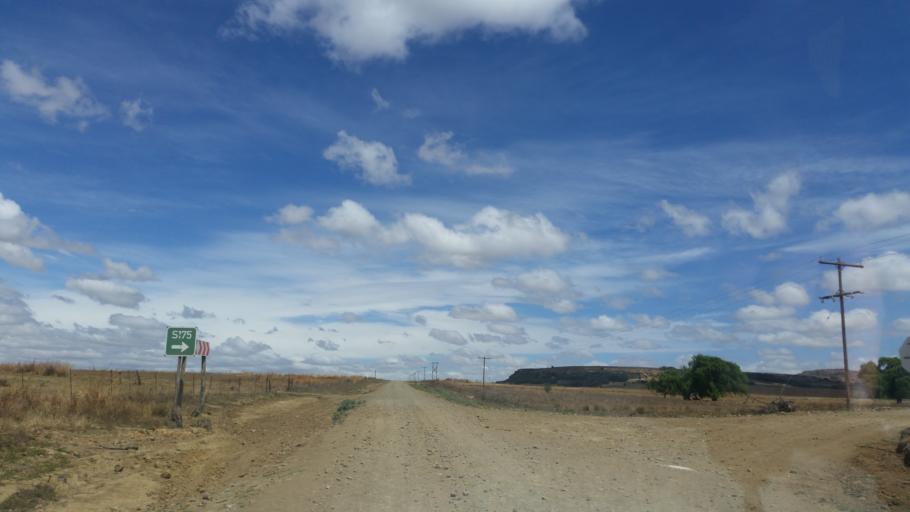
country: ZA
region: Orange Free State
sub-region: Thabo Mofutsanyana District Municipality
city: Bethlehem
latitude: -28.2182
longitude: 28.5714
